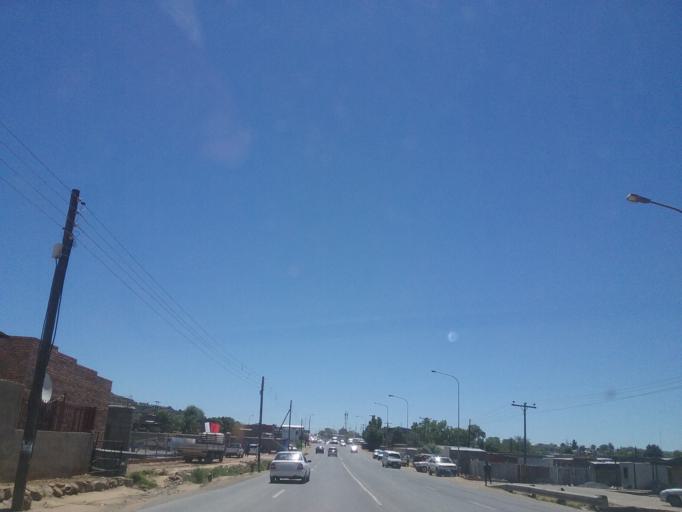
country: LS
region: Maseru
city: Nako
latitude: -29.4207
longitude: 27.7098
